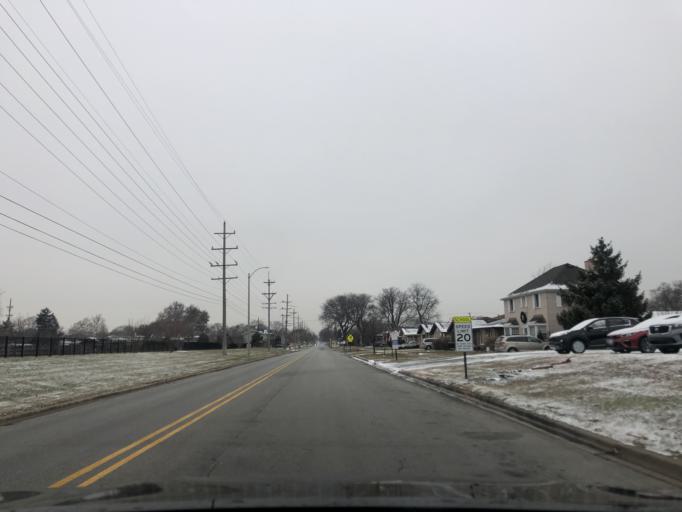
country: US
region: Illinois
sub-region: Cook County
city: Evergreen Park
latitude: 41.7282
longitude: -87.6898
